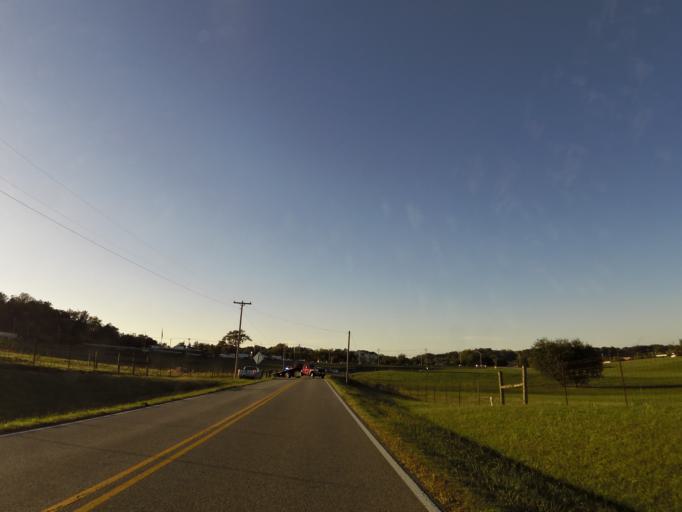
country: US
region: Tennessee
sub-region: Blount County
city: Alcoa
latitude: 35.8442
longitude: -83.9627
